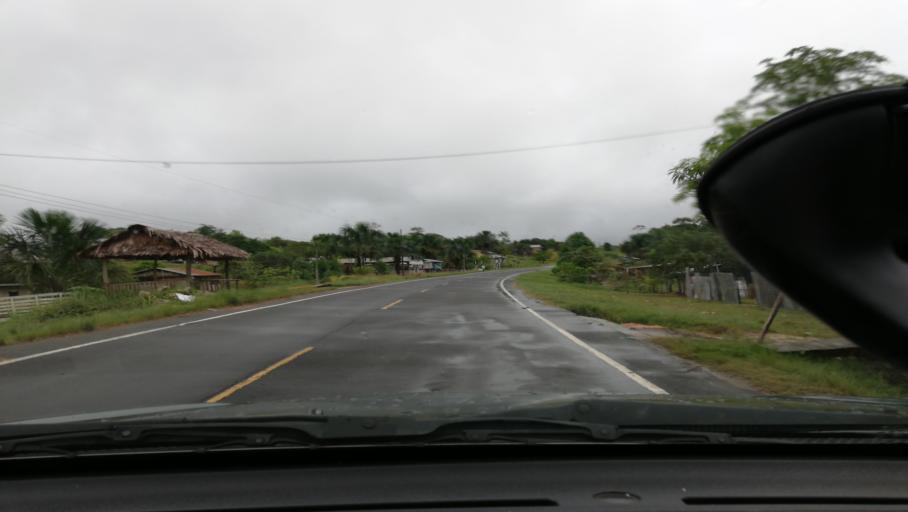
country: PE
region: Loreto
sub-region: Provincia de Loreto
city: Nauta
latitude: -4.2193
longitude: -73.4831
